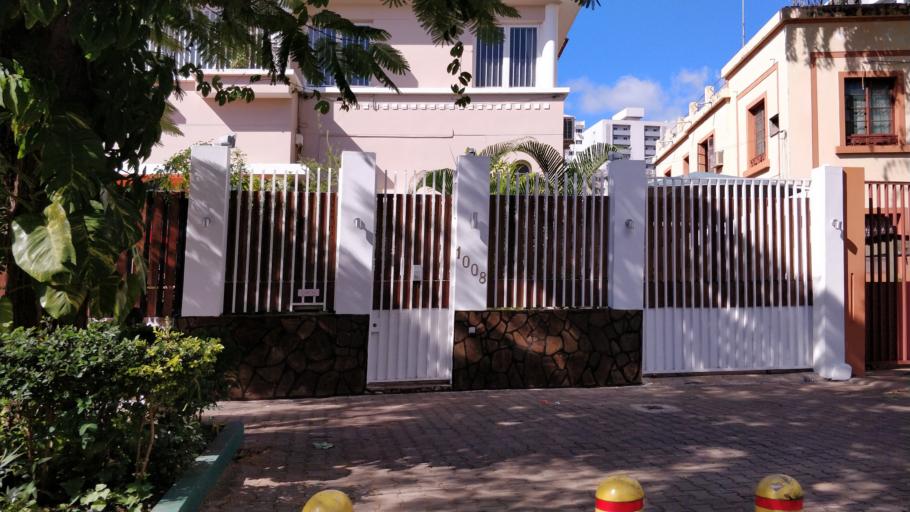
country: MZ
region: Maputo City
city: Maputo
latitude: -25.9709
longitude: 32.5932
